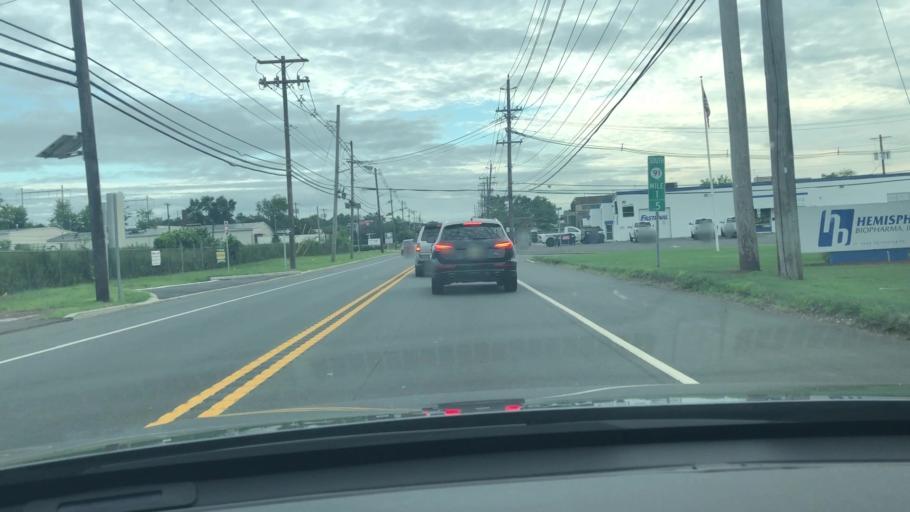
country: US
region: New Jersey
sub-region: Somerset County
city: Somerset
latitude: 40.4715
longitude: -74.4766
